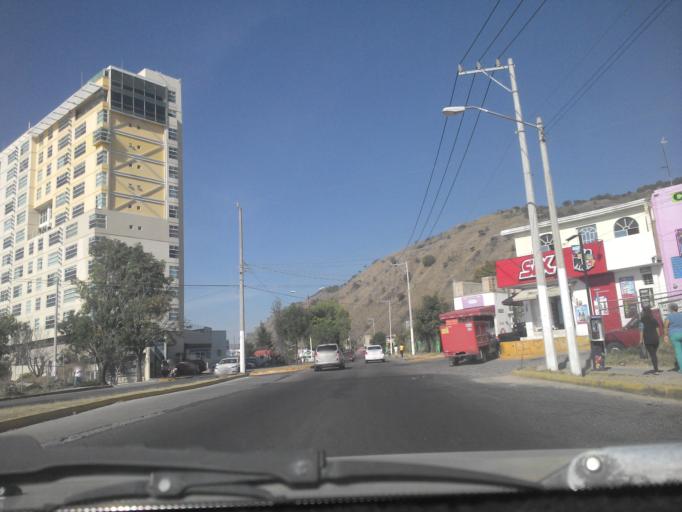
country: MX
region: Jalisco
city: Guadalajara
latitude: 20.6577
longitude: -103.4503
